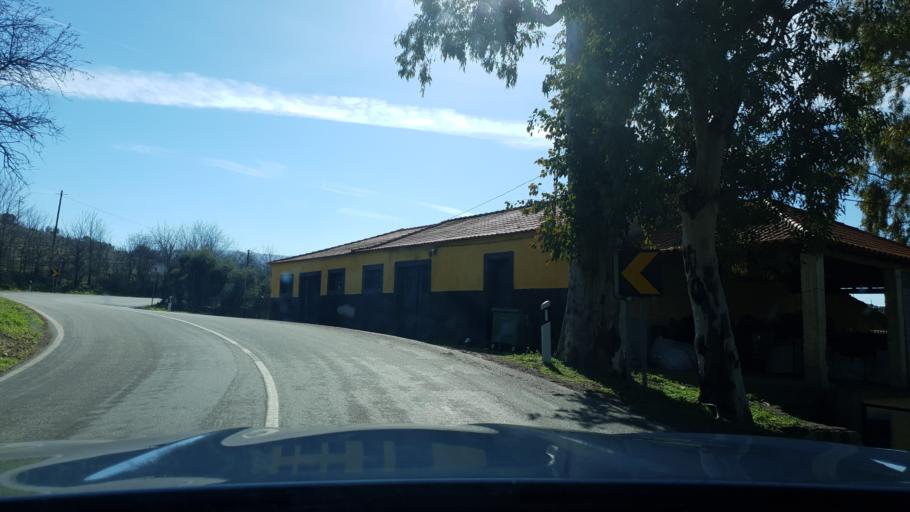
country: PT
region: Braganca
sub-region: Torre de Moncorvo
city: Torre de Moncorvo
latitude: 41.2158
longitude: -7.0922
